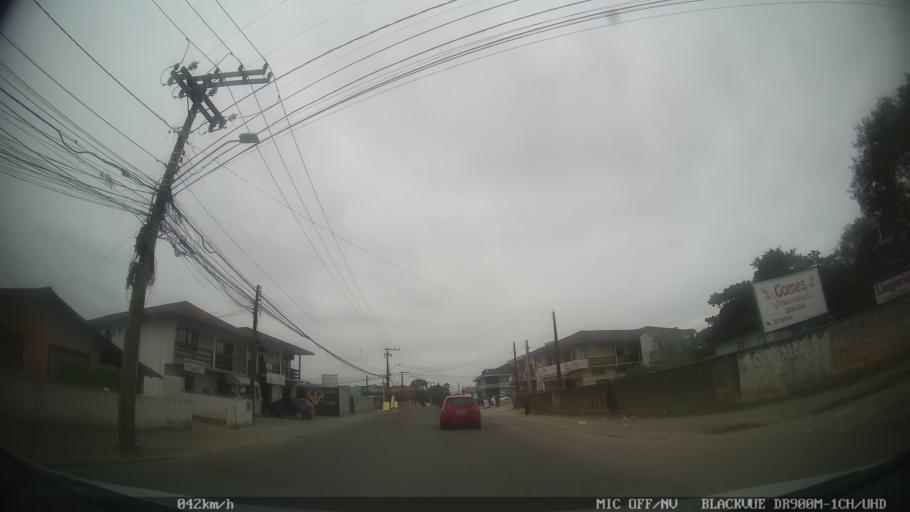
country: BR
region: Santa Catarina
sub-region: Joinville
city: Joinville
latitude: -26.3411
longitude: -48.8213
